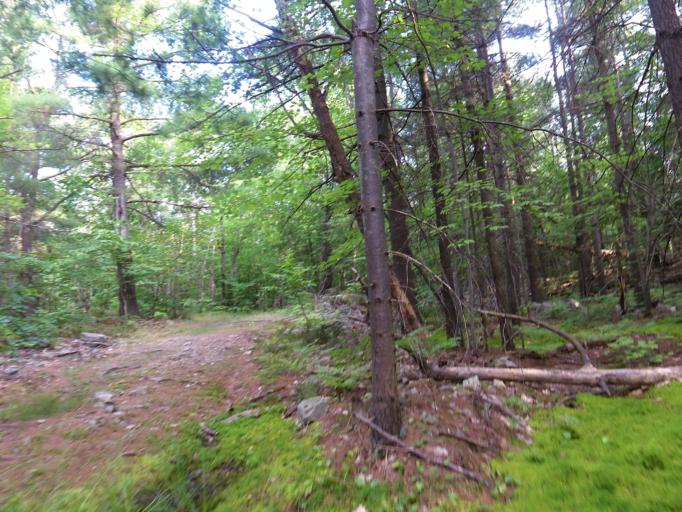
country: CA
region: Ontario
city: Bells Corners
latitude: 45.3248
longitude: -75.8602
